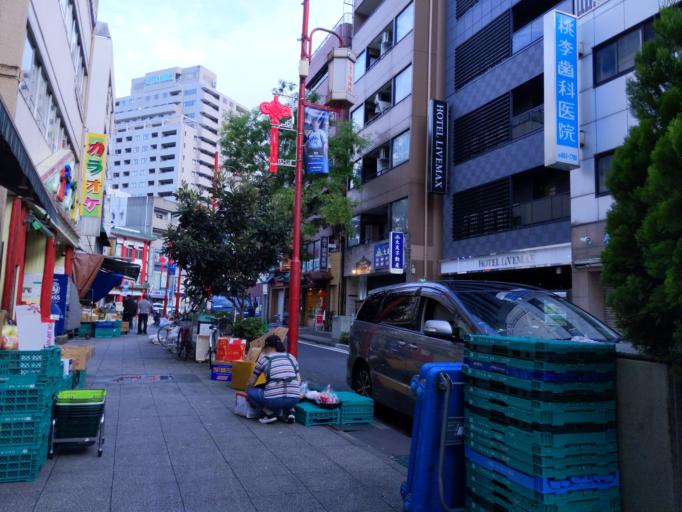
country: JP
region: Kanagawa
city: Yokohama
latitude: 35.4423
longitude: 139.6437
